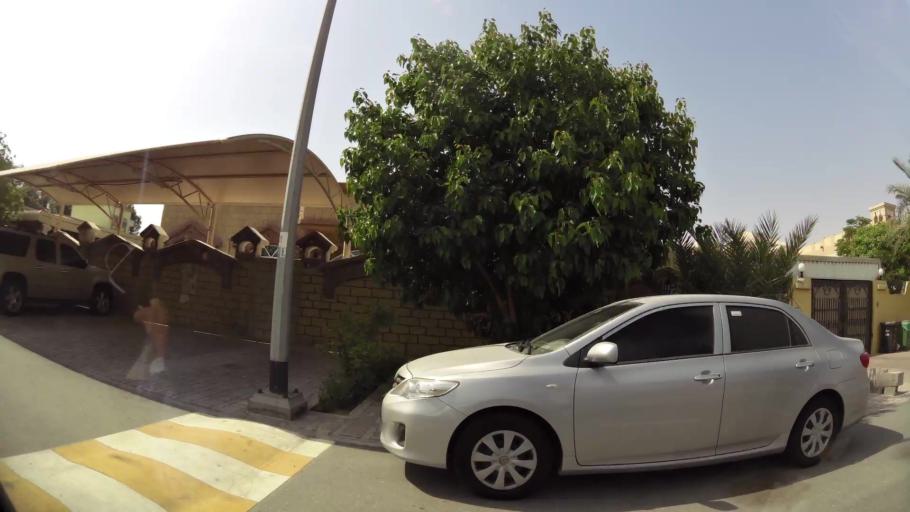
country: AE
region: Ash Shariqah
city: Sharjah
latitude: 25.2548
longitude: 55.4315
